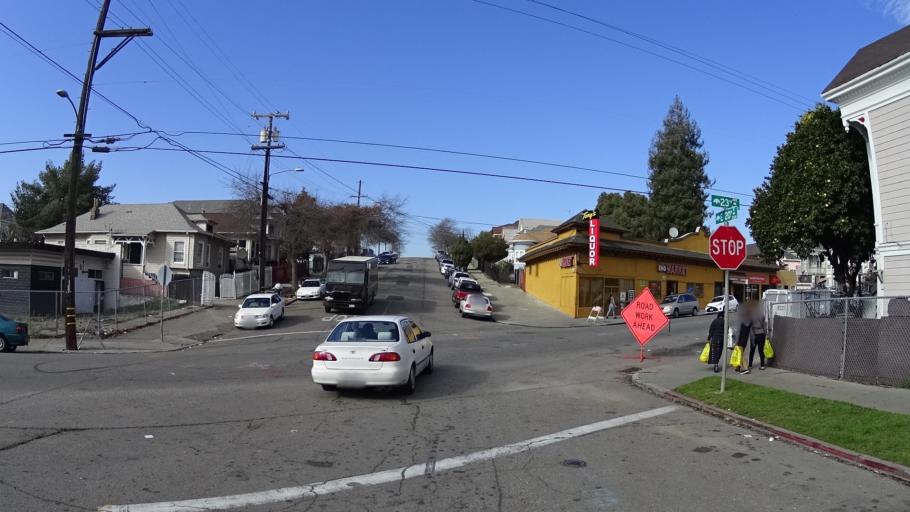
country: US
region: California
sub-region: Alameda County
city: Alameda
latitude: 37.7875
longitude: -122.2319
